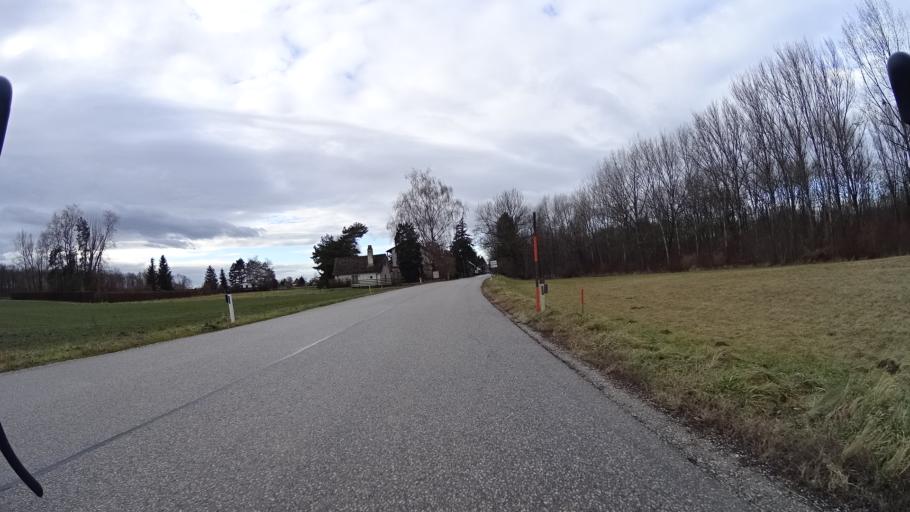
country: AT
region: Lower Austria
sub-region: Politischer Bezirk Tulln
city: Langenrohr
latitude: 48.3266
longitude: 16.0091
